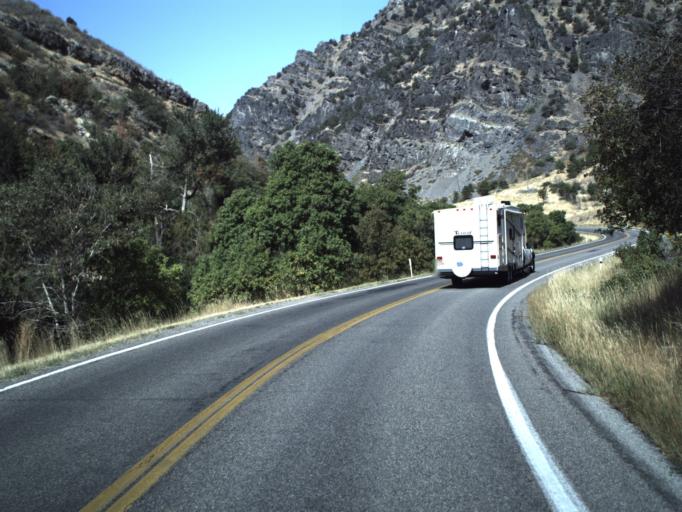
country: US
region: Utah
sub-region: Cache County
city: Hyrum
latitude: 41.6215
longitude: -111.7822
